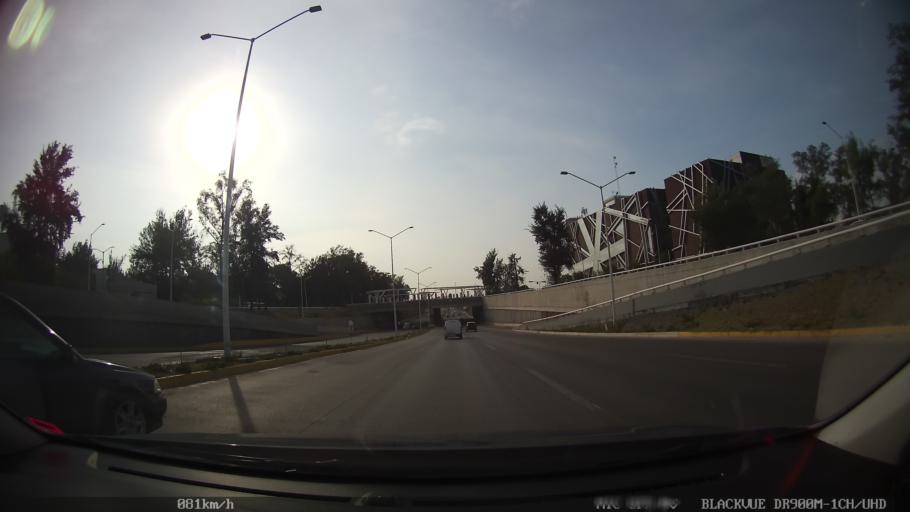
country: MX
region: Jalisco
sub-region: Zapopan
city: Zapopan
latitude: 20.7396
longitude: -103.3834
